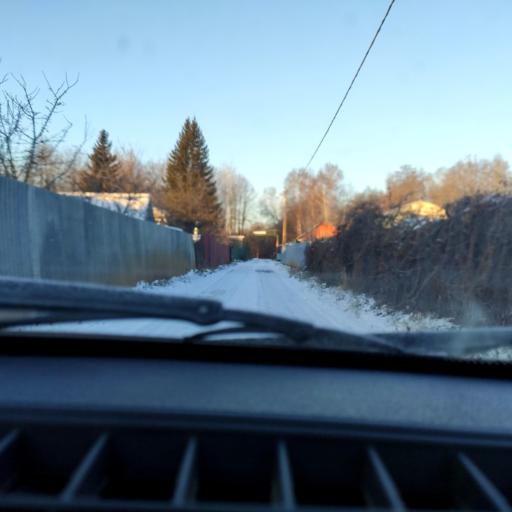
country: RU
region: Bashkortostan
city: Avdon
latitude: 54.6255
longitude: 55.7129
